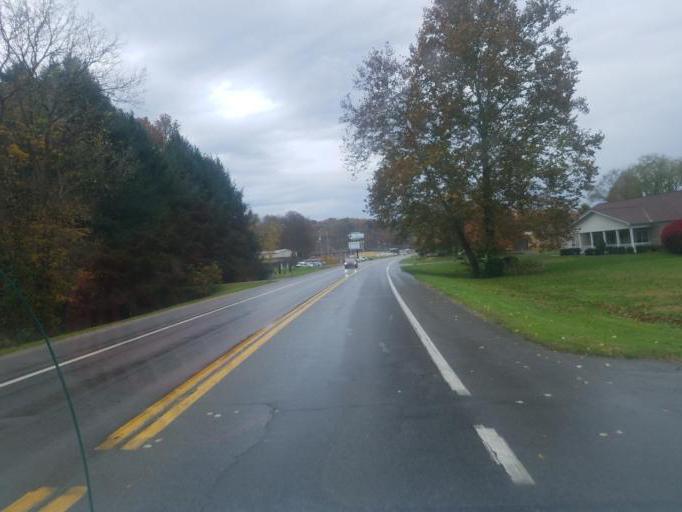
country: US
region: West Virginia
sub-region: Wood County
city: Boaz
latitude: 39.3665
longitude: -81.4859
